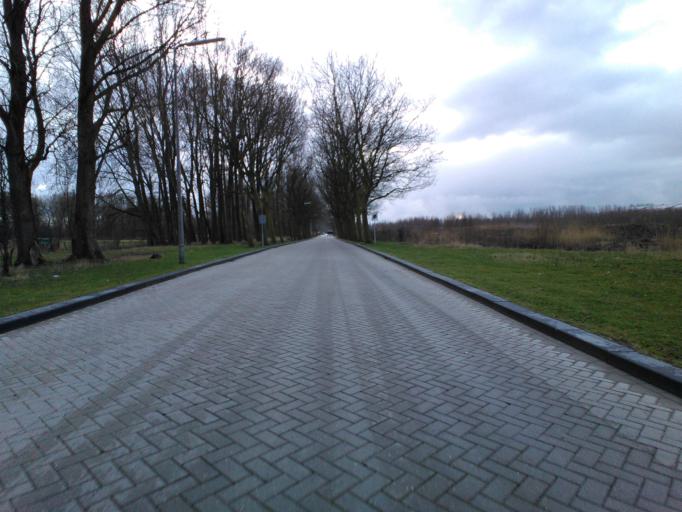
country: NL
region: South Holland
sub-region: Gemeente Delft
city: Delft
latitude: 51.9886
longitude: 4.3848
